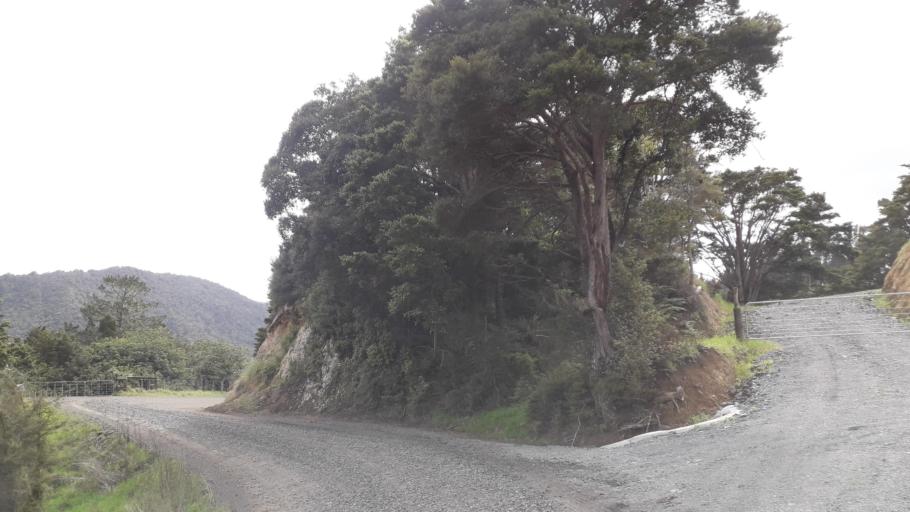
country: NZ
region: Northland
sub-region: Far North District
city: Kaitaia
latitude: -35.2277
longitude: 173.2665
